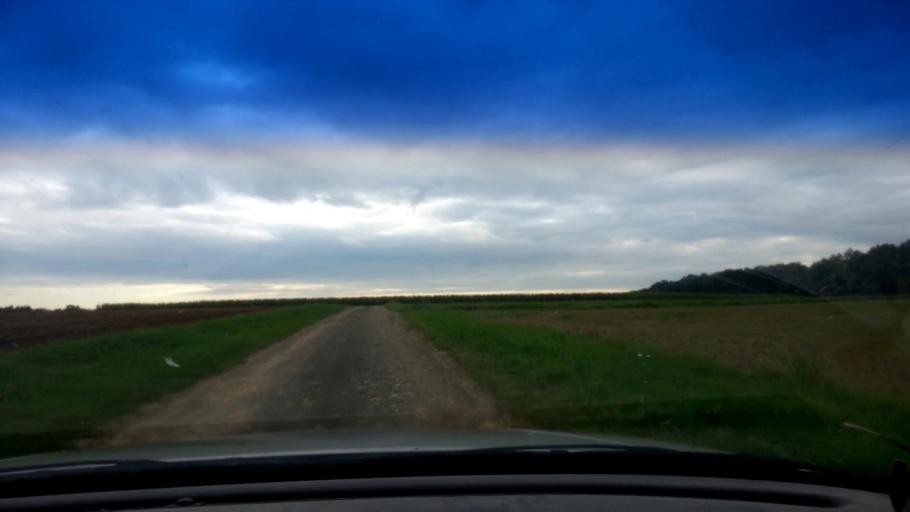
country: DE
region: Bavaria
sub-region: Upper Franconia
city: Zapfendorf
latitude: 49.9986
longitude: 10.9306
